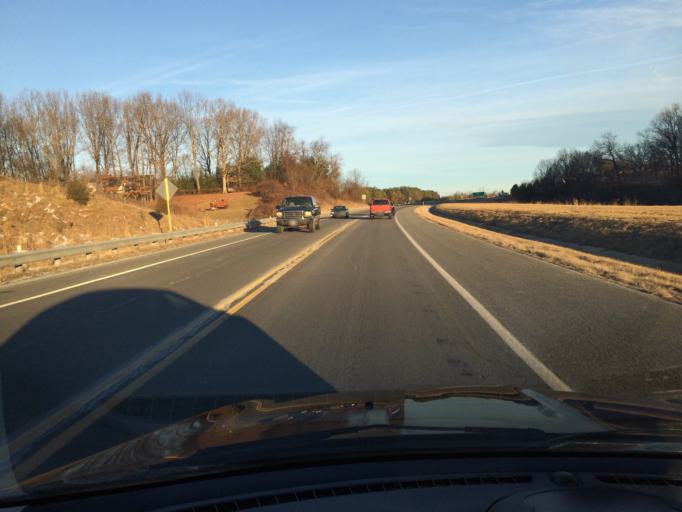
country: US
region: Virginia
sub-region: City of Staunton
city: Staunton
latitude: 38.1434
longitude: -79.1141
